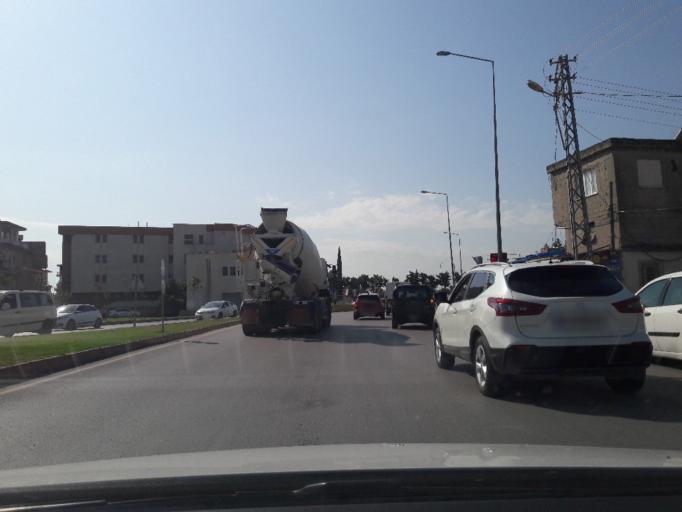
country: TR
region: Adana
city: Seyhan
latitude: 36.9946
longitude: 35.3002
